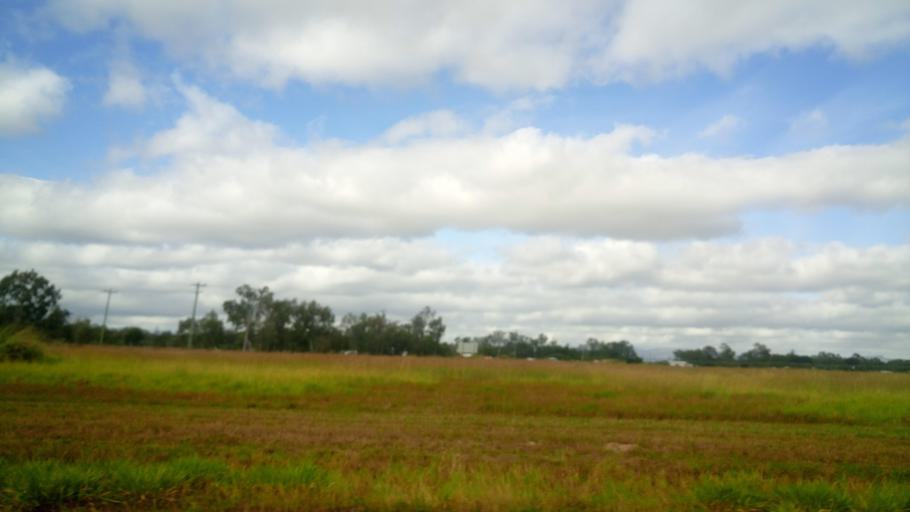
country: AU
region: Queensland
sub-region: Tablelands
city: Mareeba
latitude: -16.9793
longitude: 145.4763
